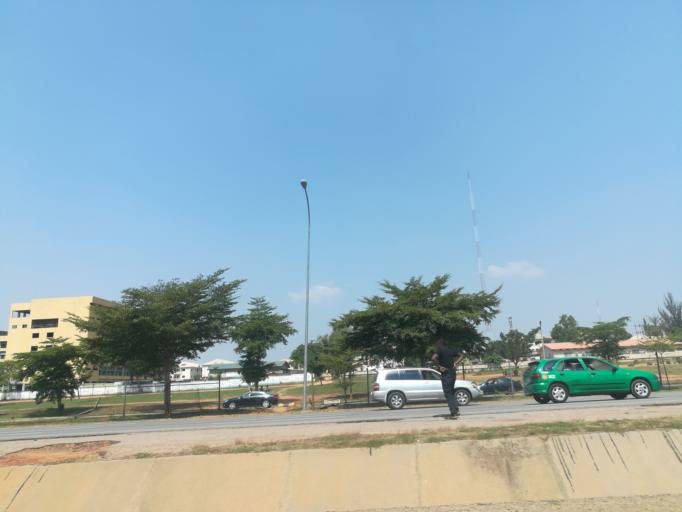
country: NG
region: Abuja Federal Capital Territory
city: Abuja
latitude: 9.0774
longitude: 7.4475
